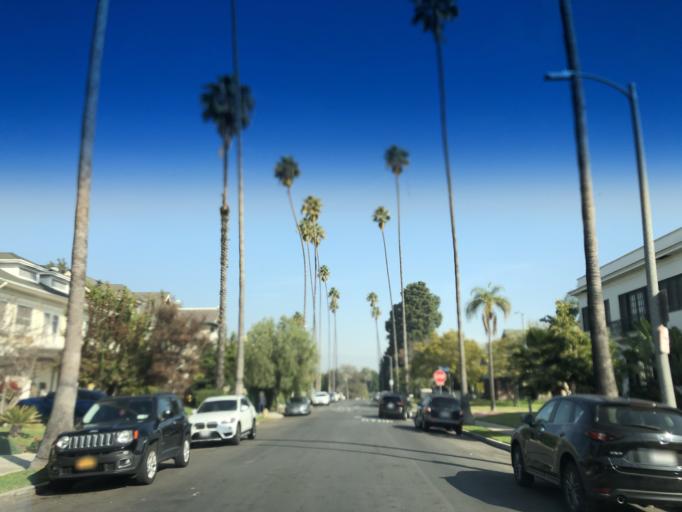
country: US
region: California
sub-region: Los Angeles County
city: Hollywood
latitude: 34.0493
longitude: -118.3192
